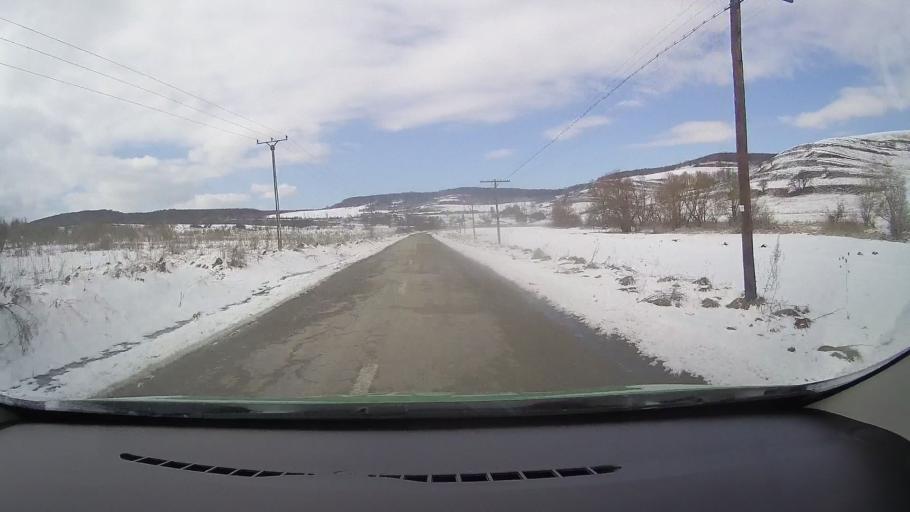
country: RO
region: Sibiu
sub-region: Comuna Altina
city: Altina
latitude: 45.9887
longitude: 24.4499
